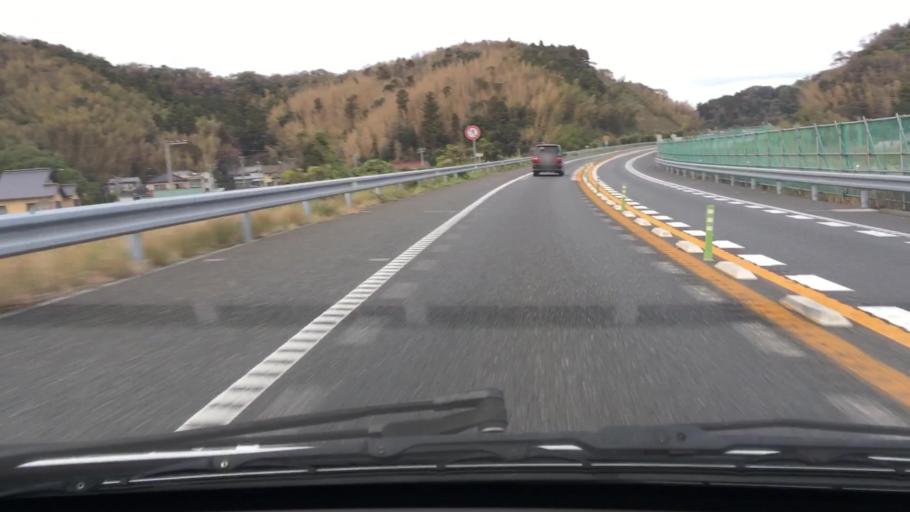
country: JP
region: Chiba
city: Kimitsu
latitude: 35.2236
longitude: 139.8844
